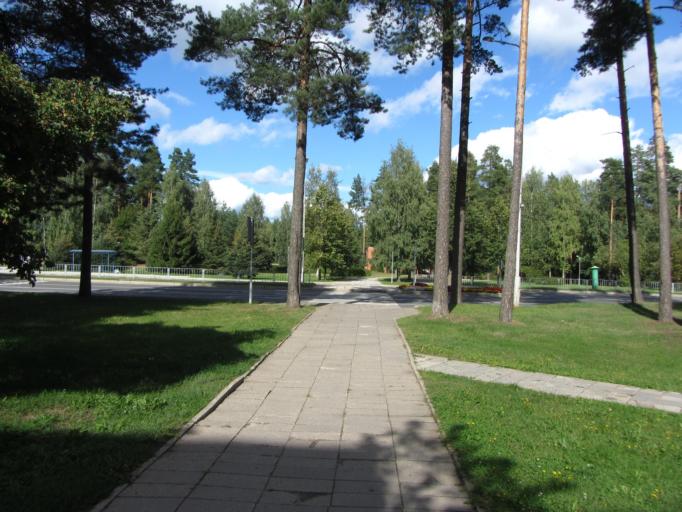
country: LT
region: Utenos apskritis
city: Visaginas
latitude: 55.6013
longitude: 26.4385
